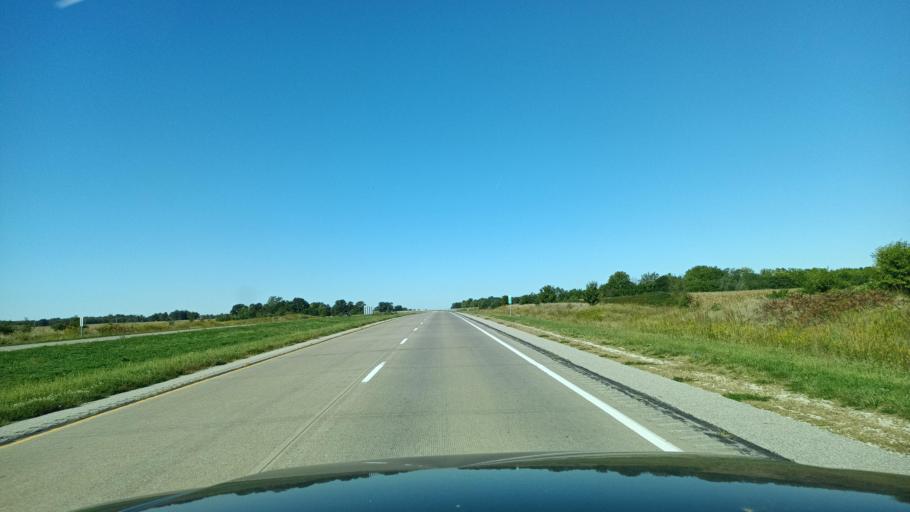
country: US
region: Iowa
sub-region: Lee County
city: Fort Madison
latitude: 40.6707
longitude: -91.2921
